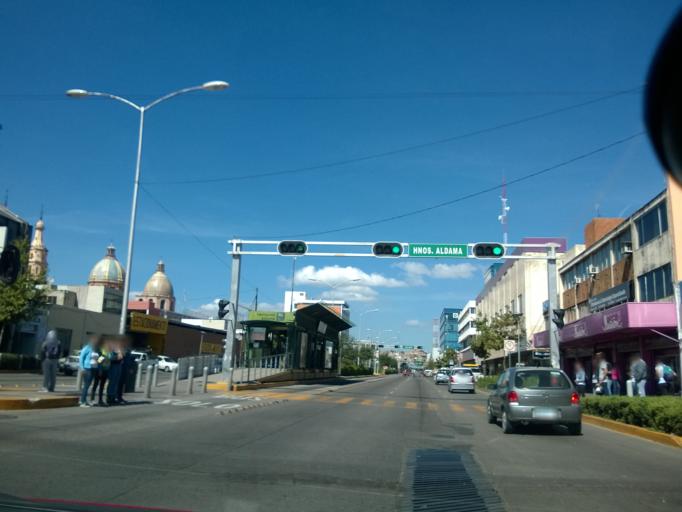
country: MX
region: Guanajuato
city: Leon
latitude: 21.1248
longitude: -101.6799
